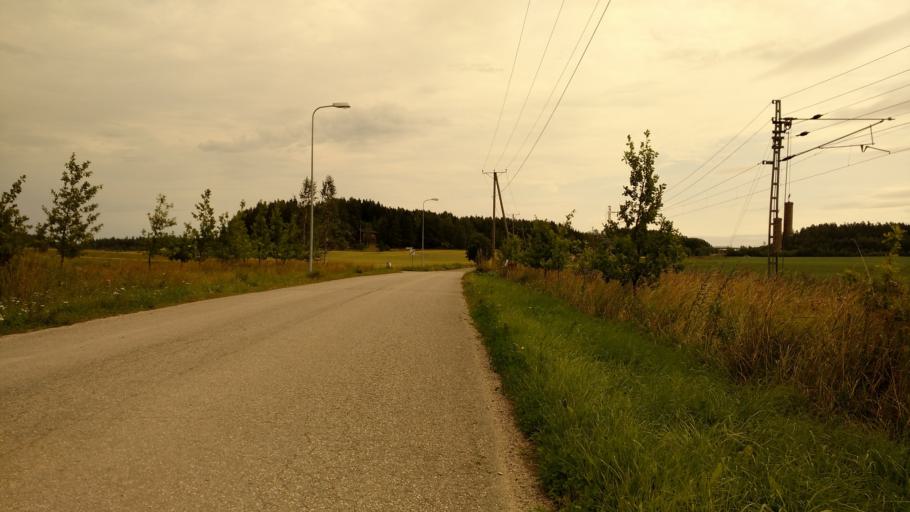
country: FI
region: Varsinais-Suomi
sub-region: Turku
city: Piikkioe
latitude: 60.4345
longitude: 22.5479
